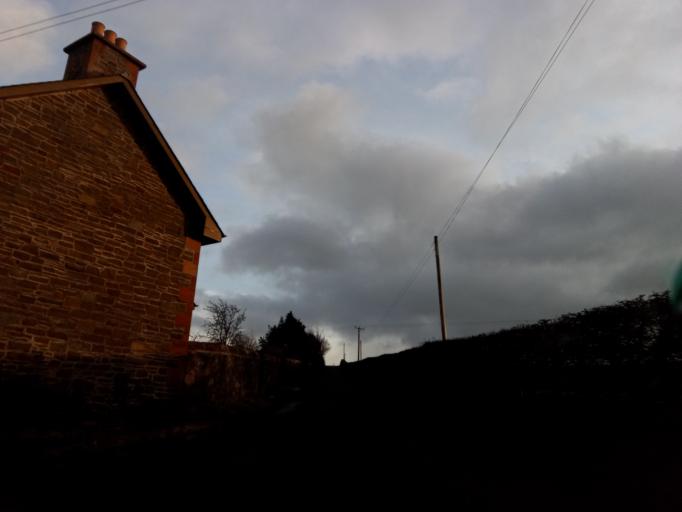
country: GB
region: Scotland
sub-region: The Scottish Borders
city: Selkirk
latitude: 55.5708
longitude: -2.8127
